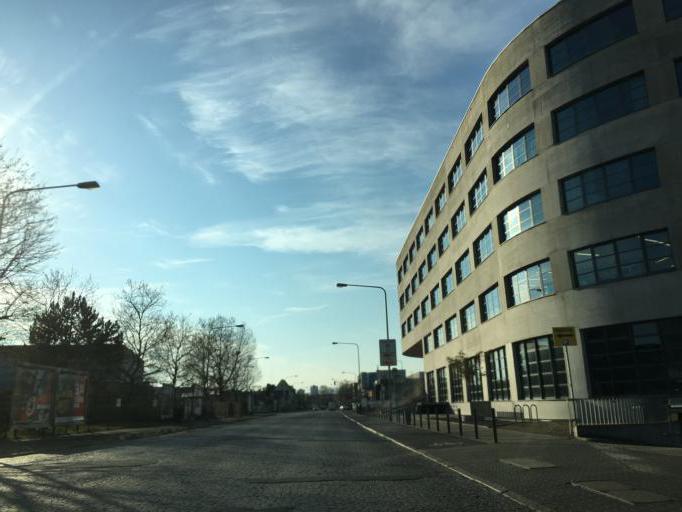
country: DE
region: Hesse
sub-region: Regierungsbezirk Darmstadt
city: Offenbach
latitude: 50.1210
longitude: 8.7515
